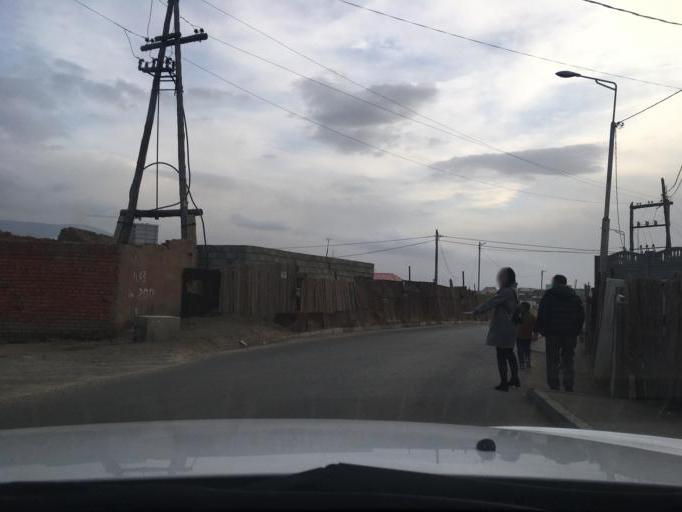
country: MN
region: Ulaanbaatar
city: Ulaanbaatar
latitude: 47.9261
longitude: 106.8574
